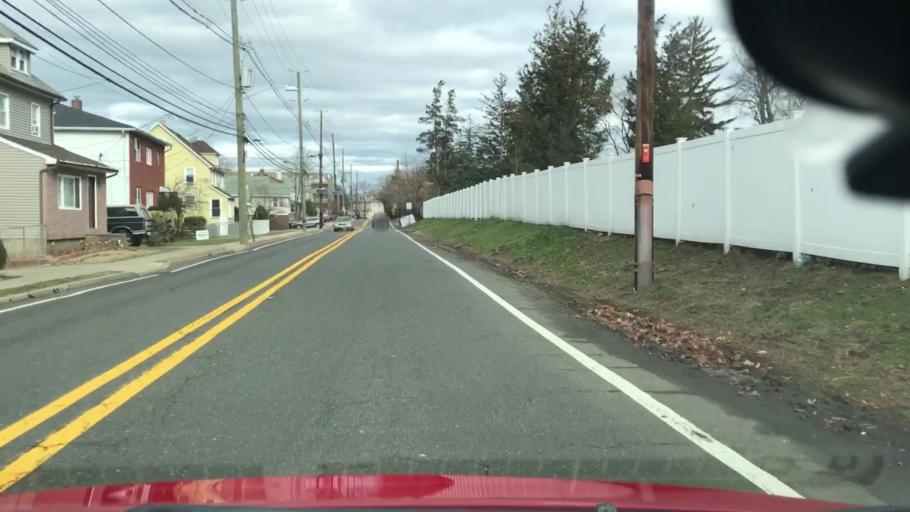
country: US
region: New Jersey
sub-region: Bergen County
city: Little Ferry
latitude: 40.8595
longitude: -74.0404
